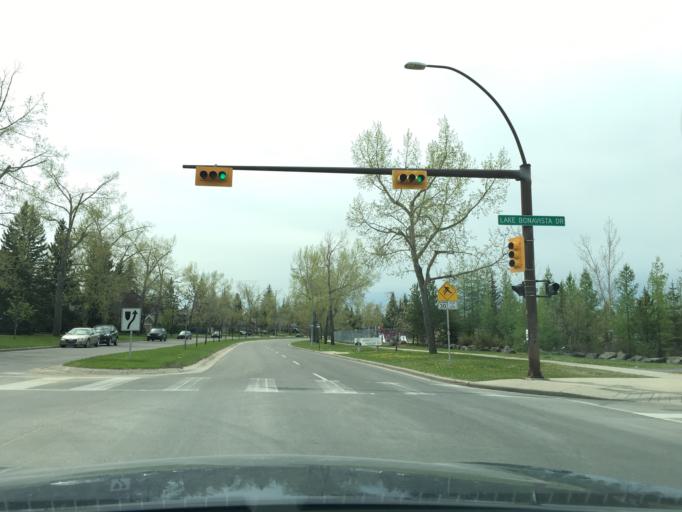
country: CA
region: Alberta
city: Calgary
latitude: 50.9463
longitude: -114.0601
